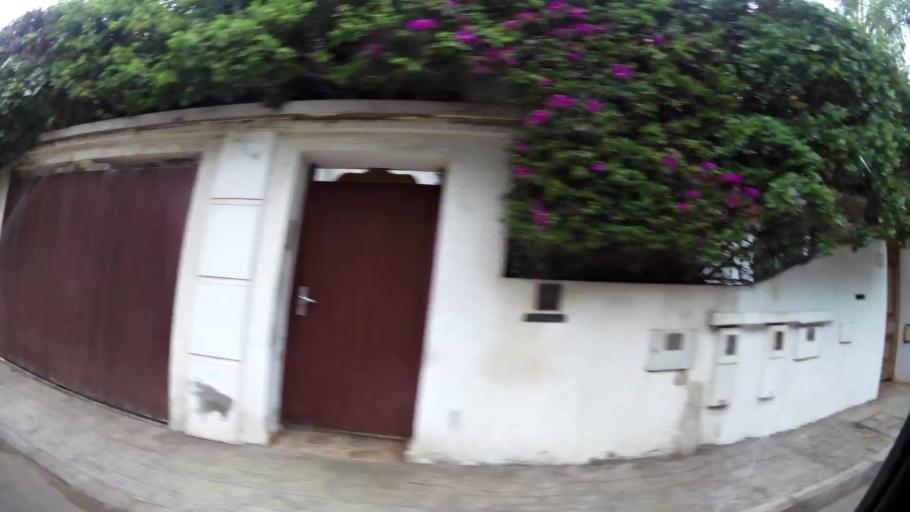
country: MA
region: Grand Casablanca
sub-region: Casablanca
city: Casablanca
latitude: 33.6001
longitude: -7.6563
